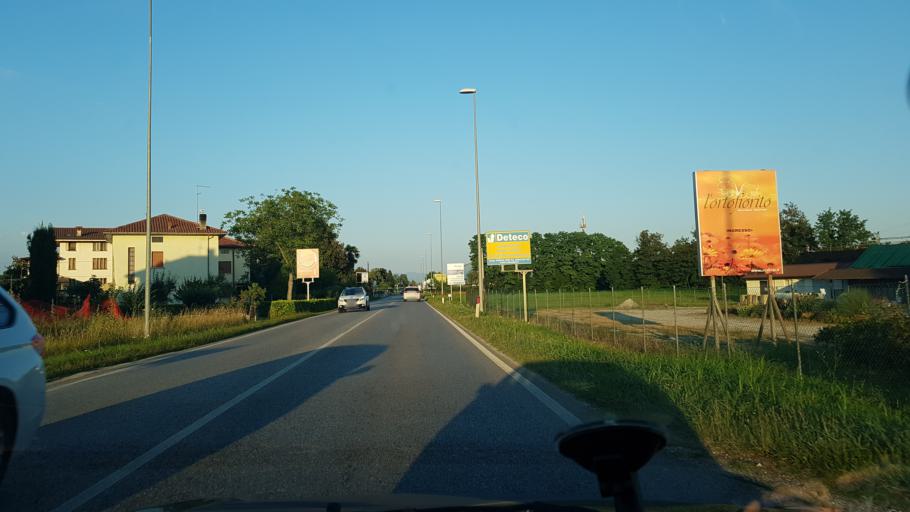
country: IT
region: Friuli Venezia Giulia
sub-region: Provincia di Udine
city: Martignacco
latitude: 46.0909
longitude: 13.1370
